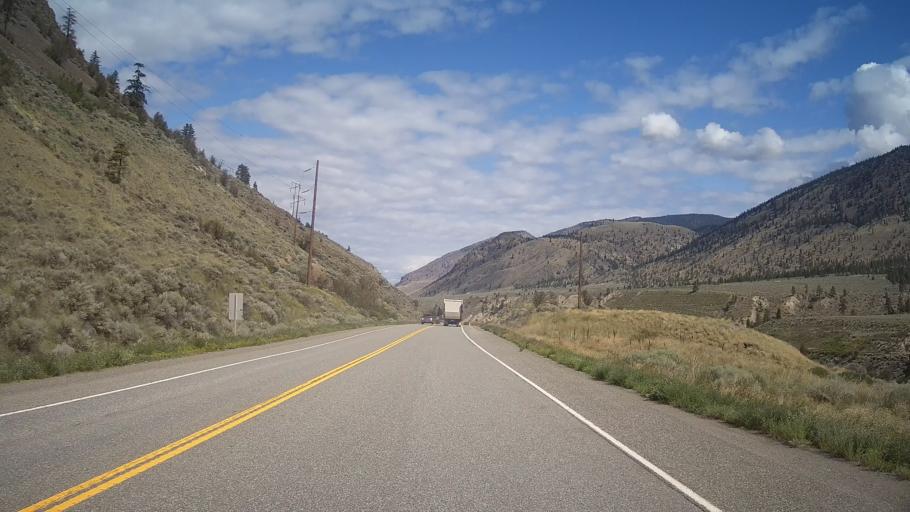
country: CA
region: British Columbia
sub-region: Thompson-Nicola Regional District
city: Ashcroft
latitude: 50.5286
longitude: -121.2856
